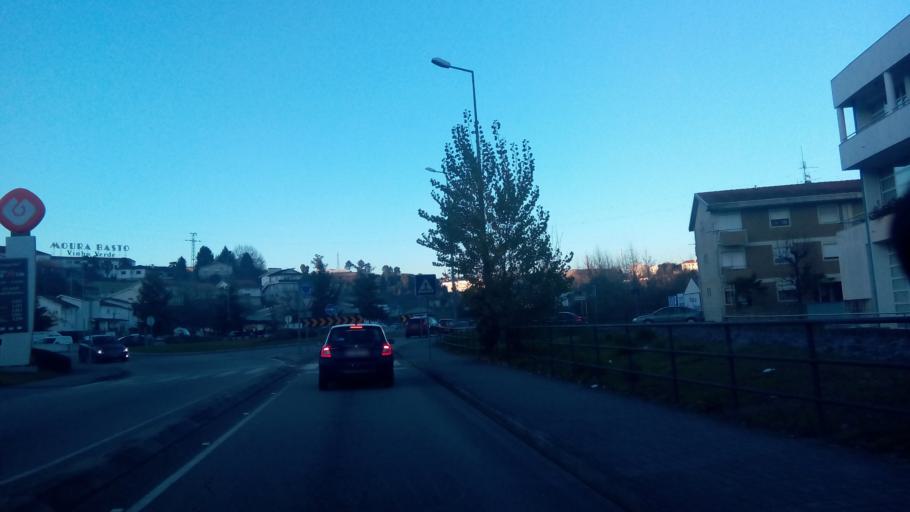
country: PT
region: Porto
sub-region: Amarante
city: Amarante
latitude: 41.2723
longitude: -8.0891
